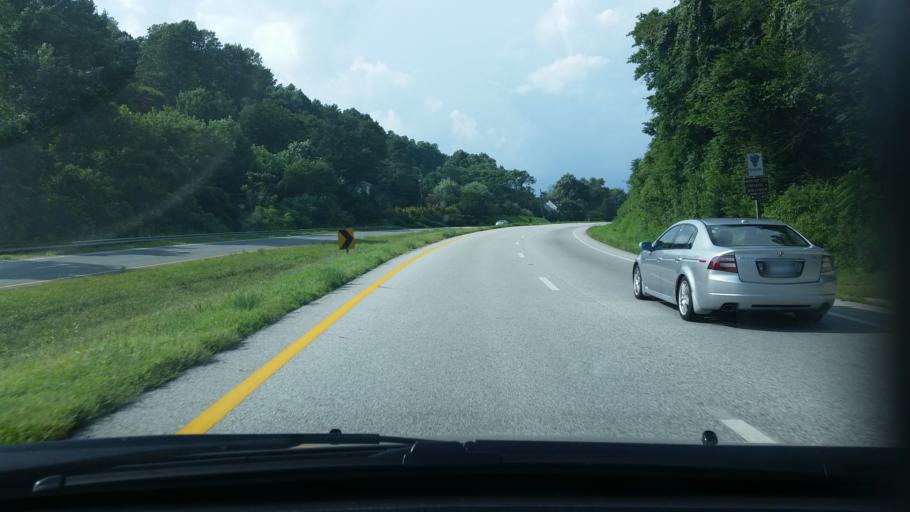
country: US
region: Virginia
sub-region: Nelson County
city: Lovingston
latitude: 37.7706
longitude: -78.8701
